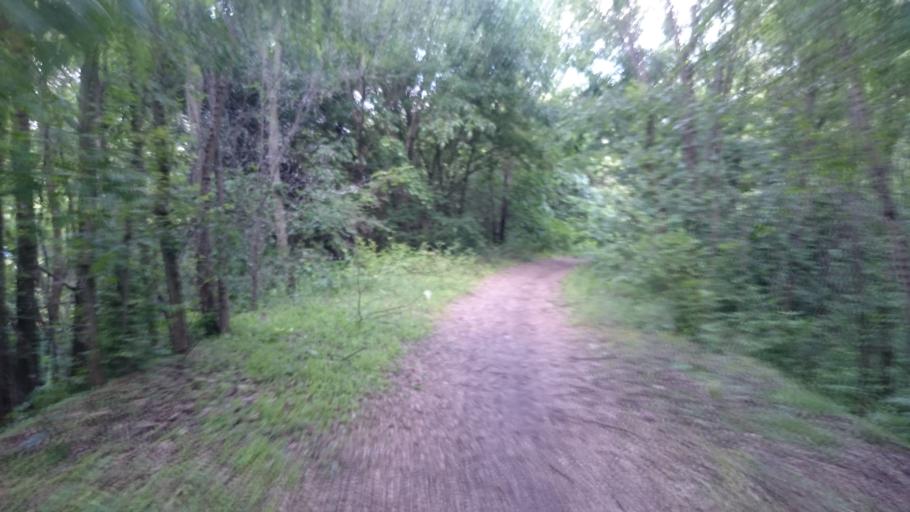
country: IT
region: Lombardy
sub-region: Provincia di Mantova
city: Mantova
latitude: 45.1379
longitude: 10.8054
